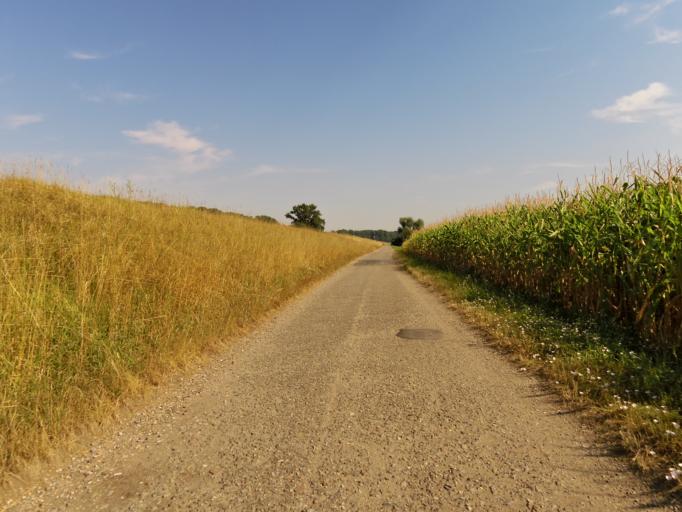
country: DE
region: Hesse
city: Lampertheim
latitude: 49.5514
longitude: 8.4226
